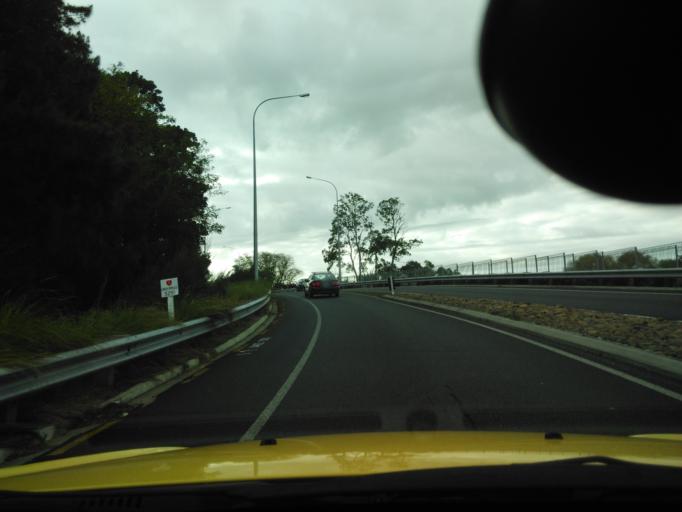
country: NZ
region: Waikato
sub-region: Waikato District
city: Ngaruawahia
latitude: -37.6120
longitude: 175.1879
